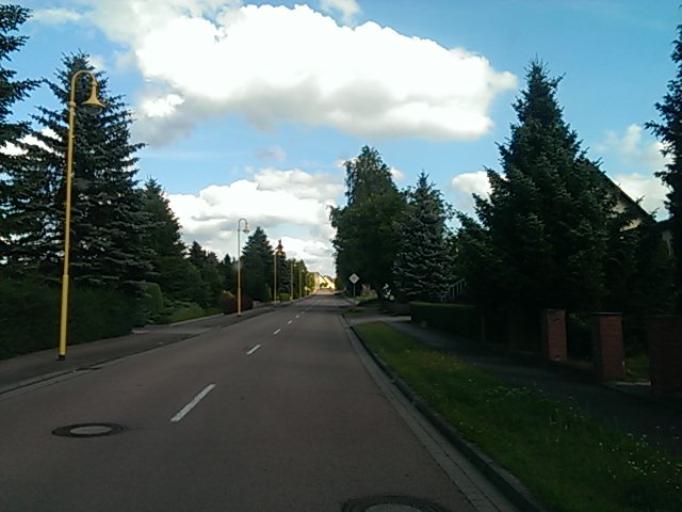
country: DE
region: Saxony-Anhalt
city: Nudersdorf
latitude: 51.9640
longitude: 12.5275
